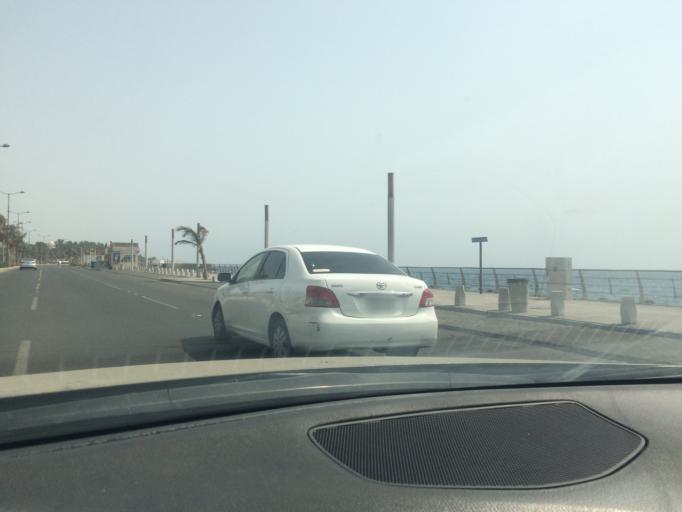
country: SA
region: Makkah
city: Jeddah
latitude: 21.5674
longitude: 39.1102
